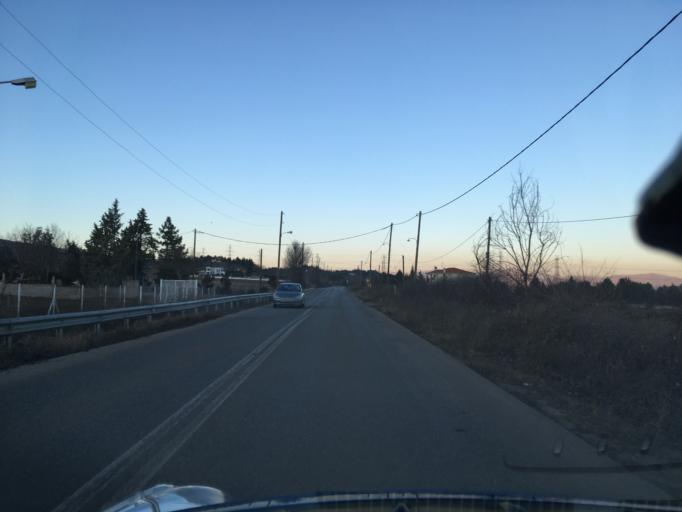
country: GR
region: West Macedonia
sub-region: Nomos Kozanis
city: Kozani
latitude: 40.2570
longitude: 21.7585
